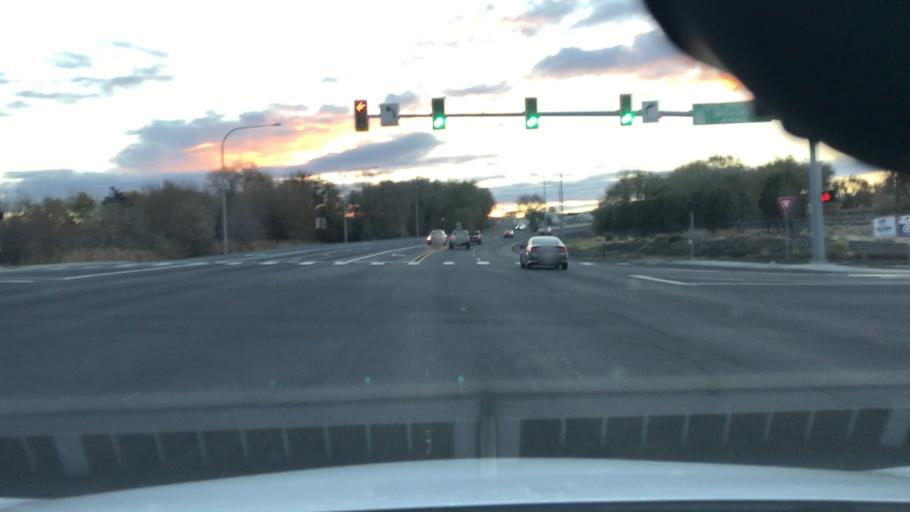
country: US
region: Washington
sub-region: Grant County
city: Moses Lake
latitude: 47.1397
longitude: -119.2624
